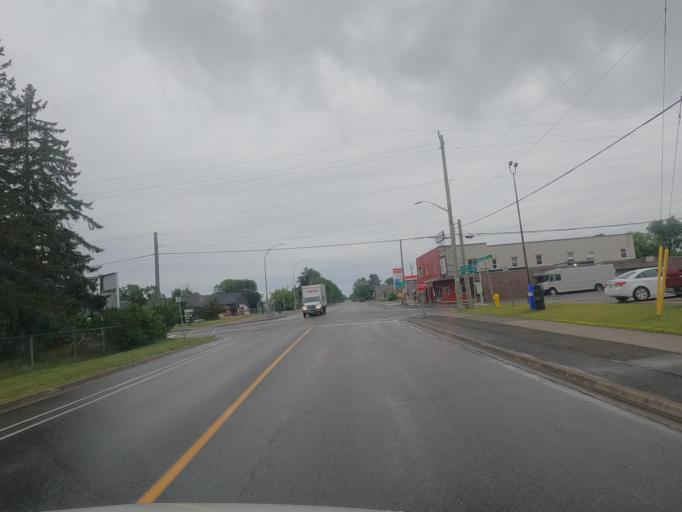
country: CA
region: Ontario
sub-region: Thunder Bay District
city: Thunder Bay
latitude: 48.4693
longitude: -89.1823
